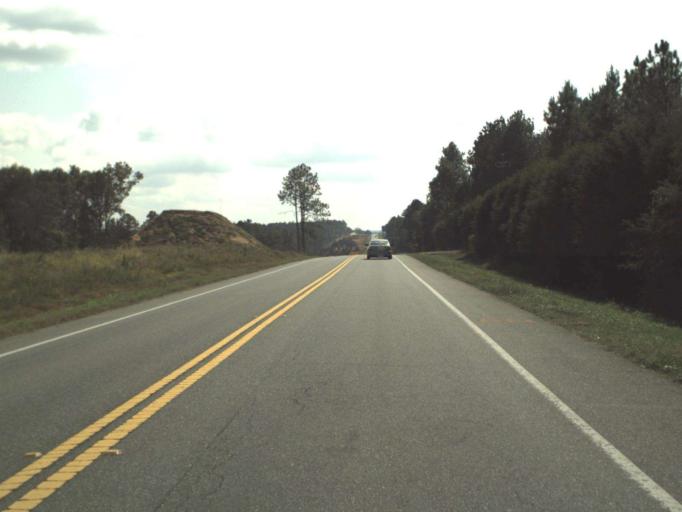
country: US
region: Florida
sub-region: Holmes County
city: Bonifay
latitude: 30.7212
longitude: -85.6857
